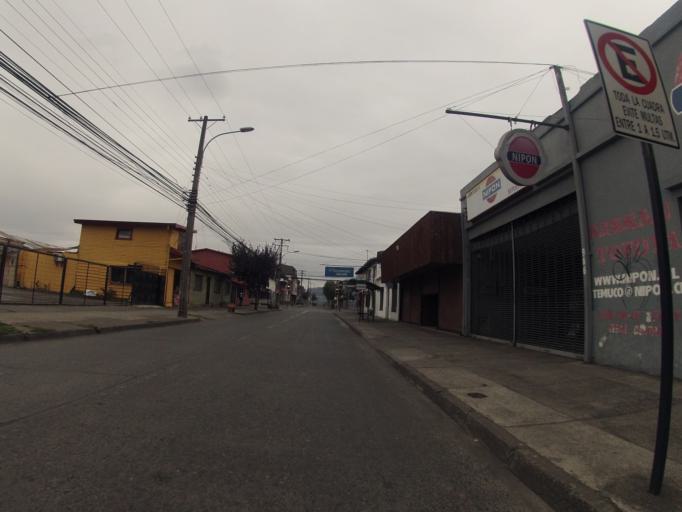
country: CL
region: Araucania
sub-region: Provincia de Cautin
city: Temuco
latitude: -38.7417
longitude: -72.5891
